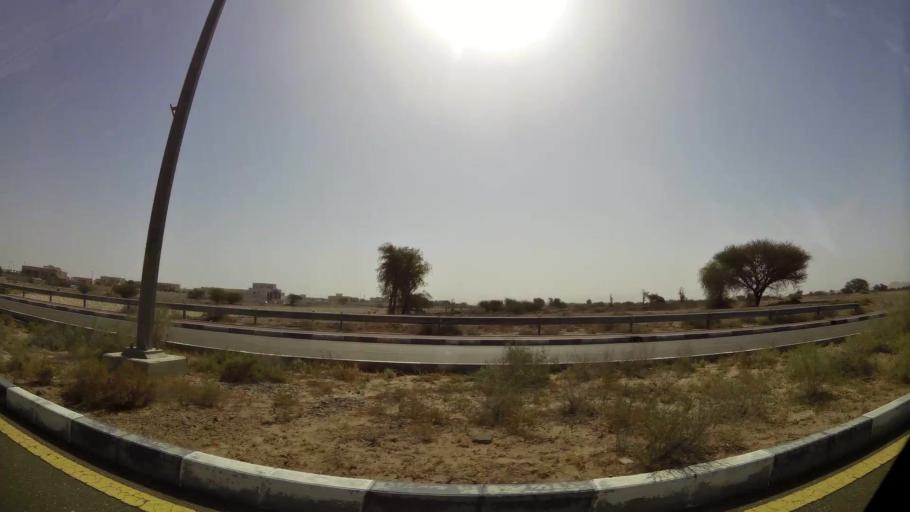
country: OM
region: Al Buraimi
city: Al Buraymi
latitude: 24.3238
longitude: 55.7847
